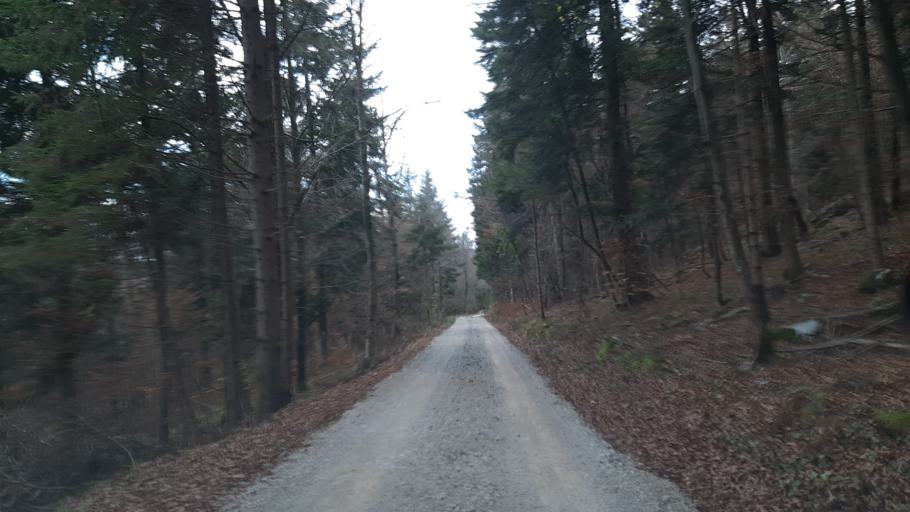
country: SI
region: Borovnica
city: Borovnica
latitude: 45.9312
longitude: 14.3817
